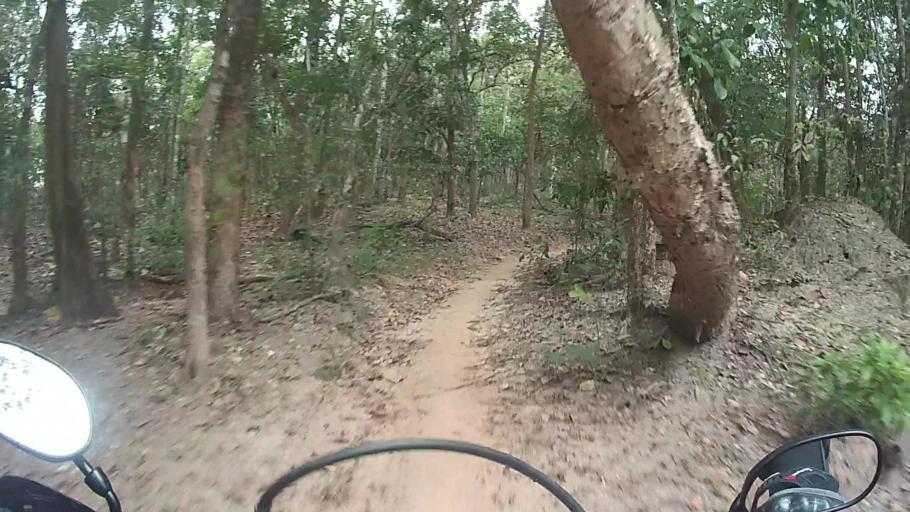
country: TH
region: Chiang Mai
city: Mae On
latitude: 18.7623
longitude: 99.3202
